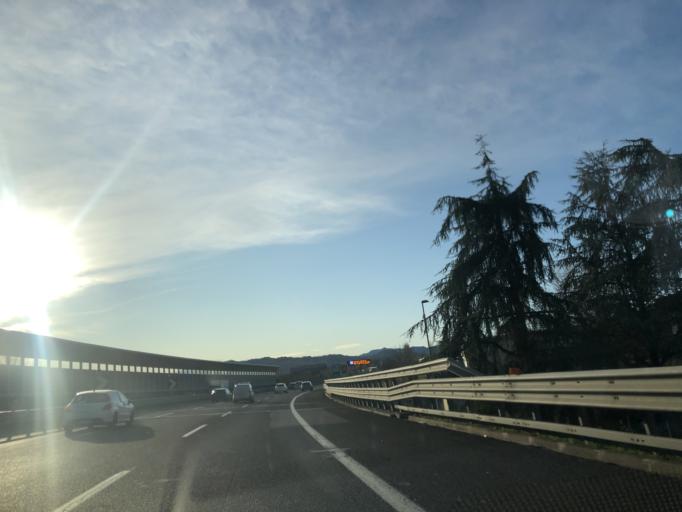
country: IT
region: Emilia-Romagna
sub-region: Provincia di Bologna
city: Casalecchio di Reno
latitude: 44.4688
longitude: 11.2738
